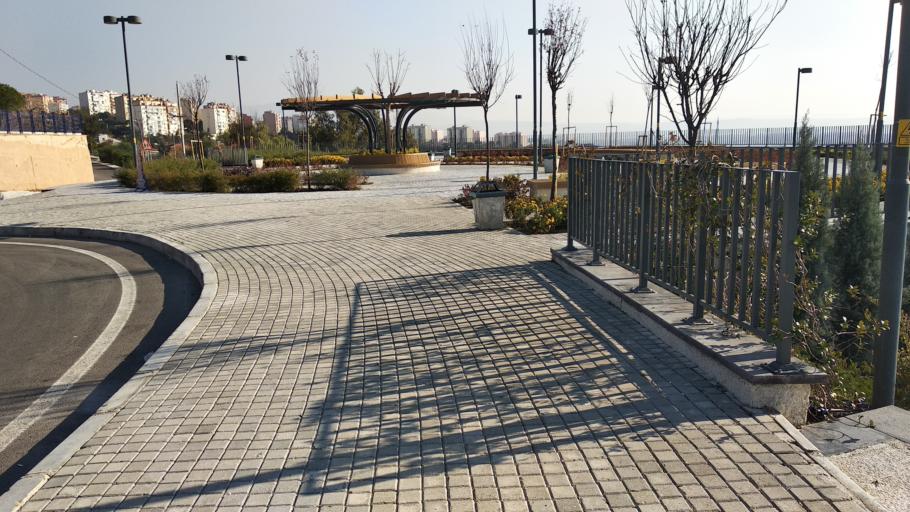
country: TR
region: Izmir
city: Karsiyaka
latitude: 38.4970
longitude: 27.0796
